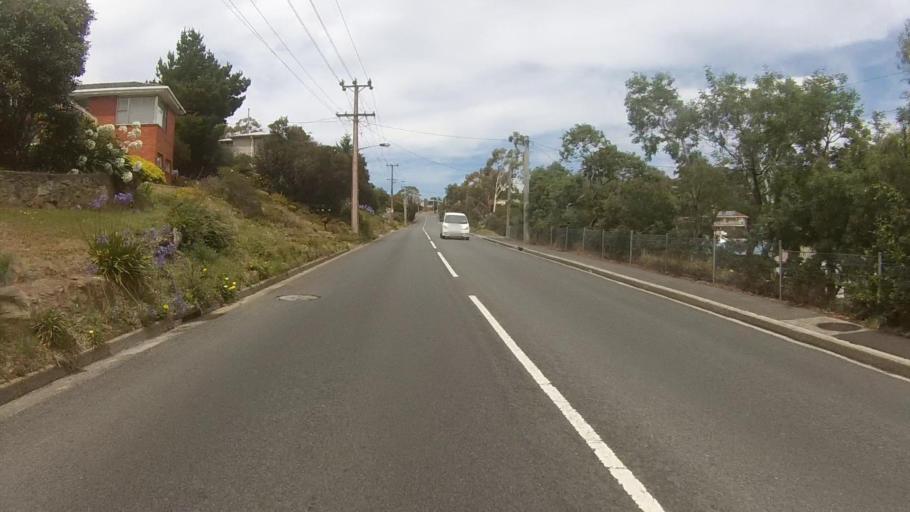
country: AU
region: Tasmania
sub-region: Clarence
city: Lindisfarne
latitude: -42.8526
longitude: 147.3704
